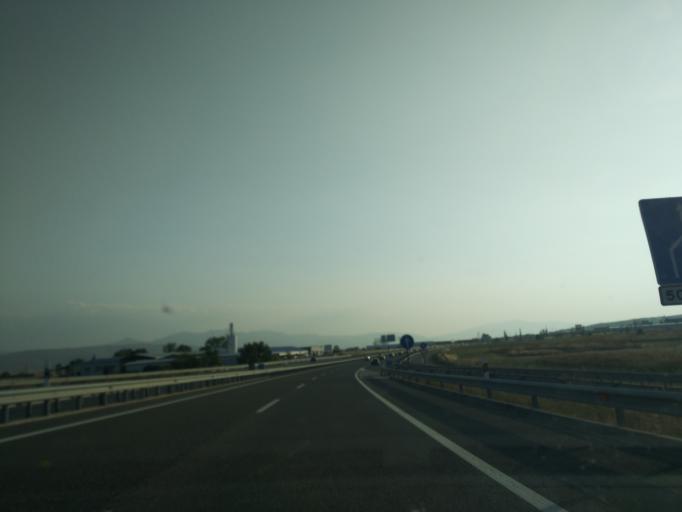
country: ES
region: Castille and Leon
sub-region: Provincia de Avila
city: Avila
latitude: 40.6468
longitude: -4.7286
